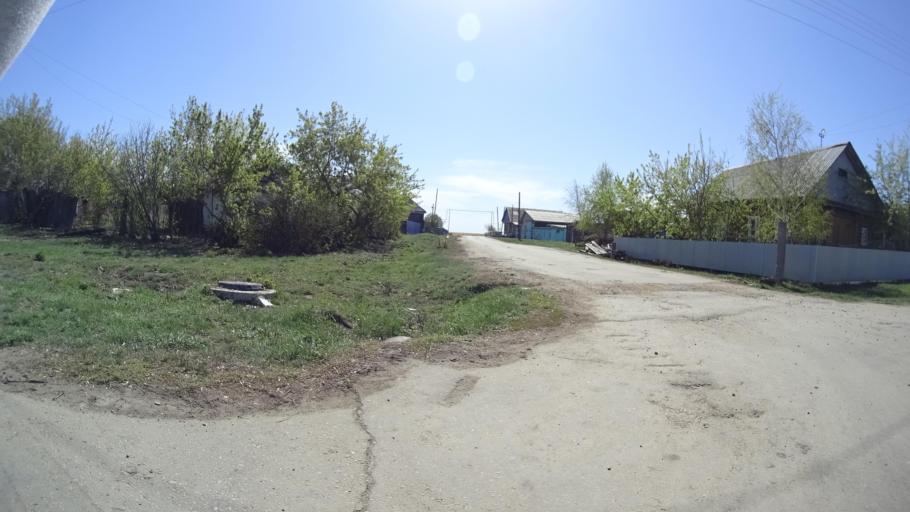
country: RU
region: Chelyabinsk
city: Chesma
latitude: 53.7989
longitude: 61.0229
